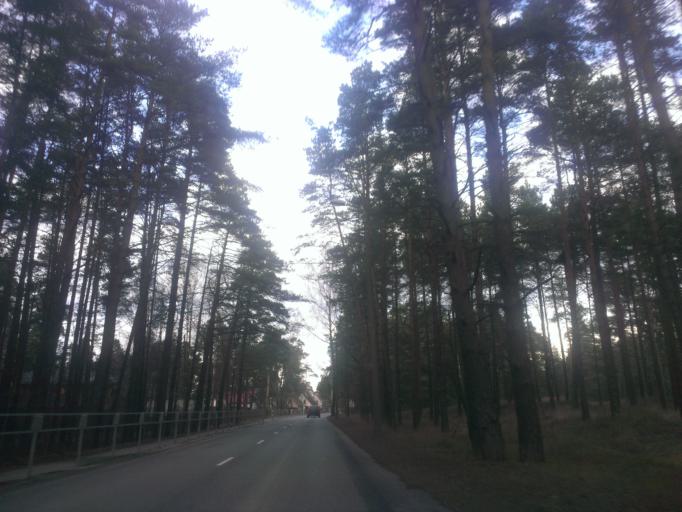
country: LV
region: Riga
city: Bolderaja
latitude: 57.0460
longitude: 24.1020
